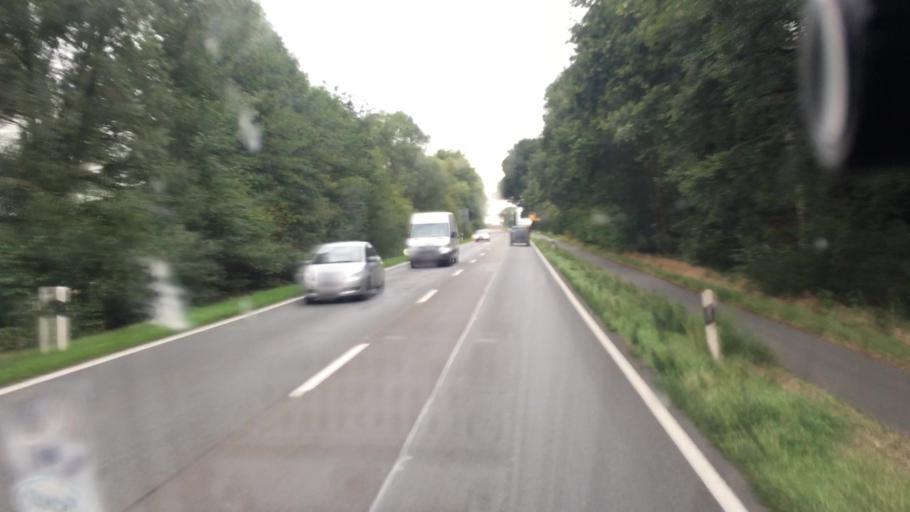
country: DE
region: Lower Saxony
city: Lohne
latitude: 52.6596
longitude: 8.1852
